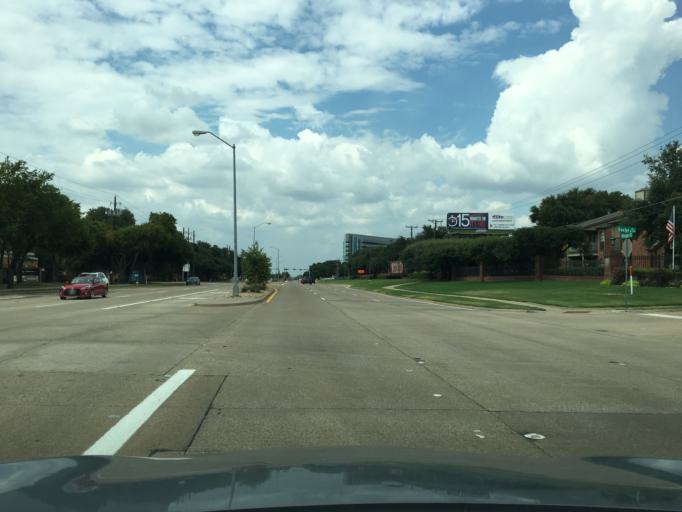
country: US
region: Texas
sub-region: Dallas County
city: Addison
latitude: 33.0188
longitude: -96.7952
